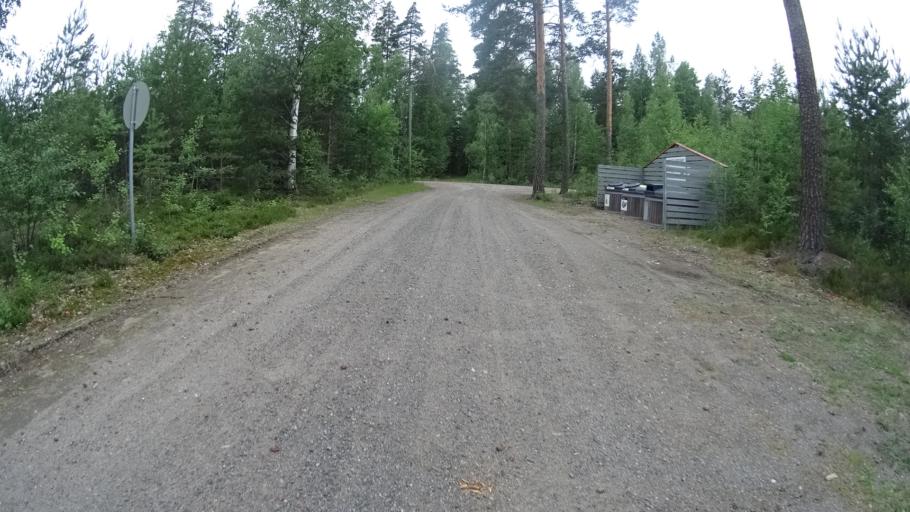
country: FI
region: Uusimaa
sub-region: Helsinki
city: Karkkila
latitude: 60.5955
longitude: 24.1229
